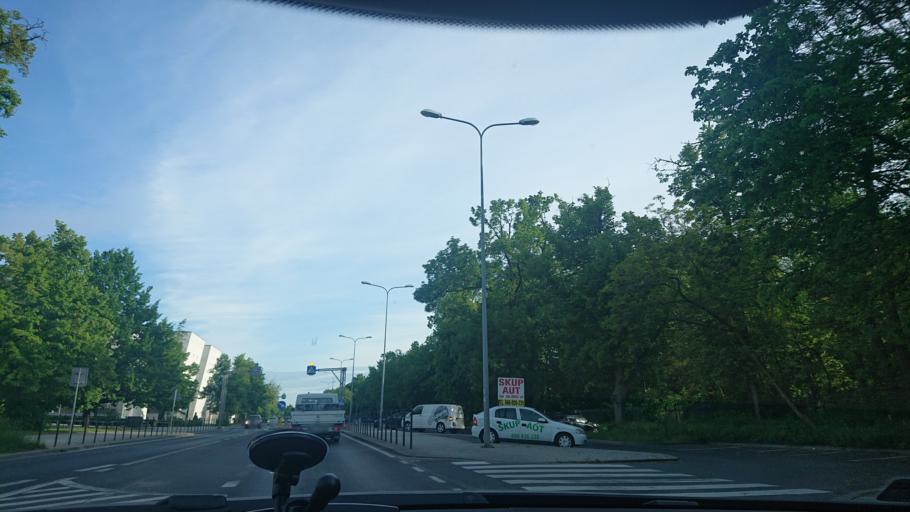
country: PL
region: Greater Poland Voivodeship
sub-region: Powiat gnieznienski
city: Gniezno
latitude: 52.5340
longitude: 17.5825
